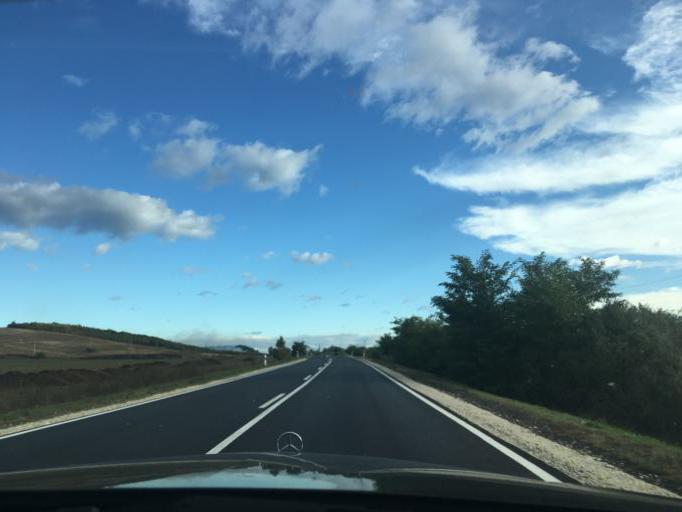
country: HU
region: Borsod-Abauj-Zemplen
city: Encs
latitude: 48.3914
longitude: 21.1588
